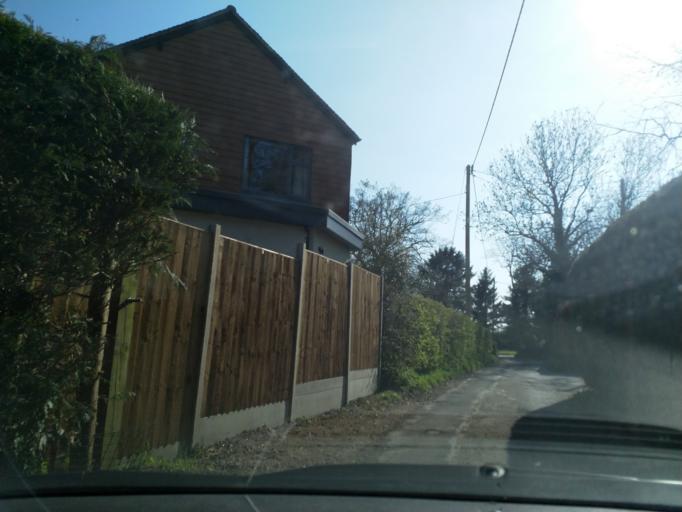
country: GB
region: England
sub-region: Warwickshire
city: Wroxall
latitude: 52.2951
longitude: -1.6922
